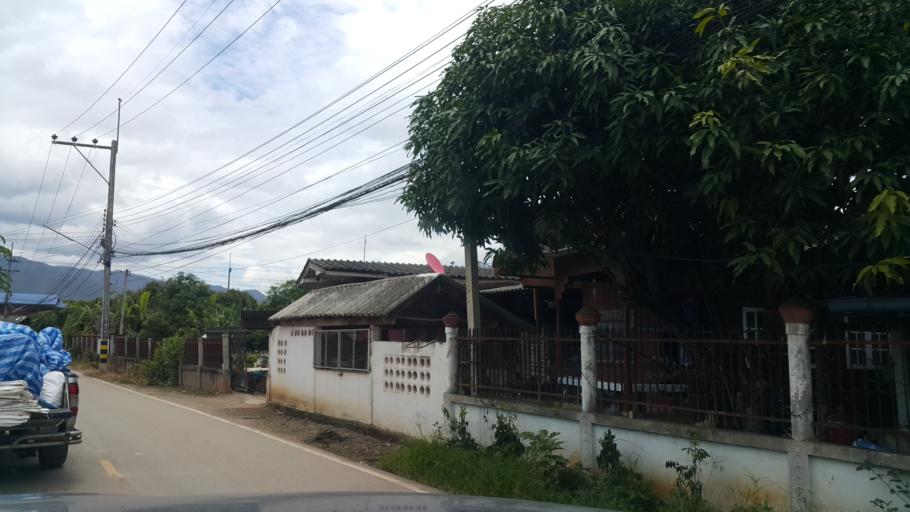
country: TH
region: Chiang Mai
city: Mae Taeng
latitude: 19.1877
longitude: 98.9891
